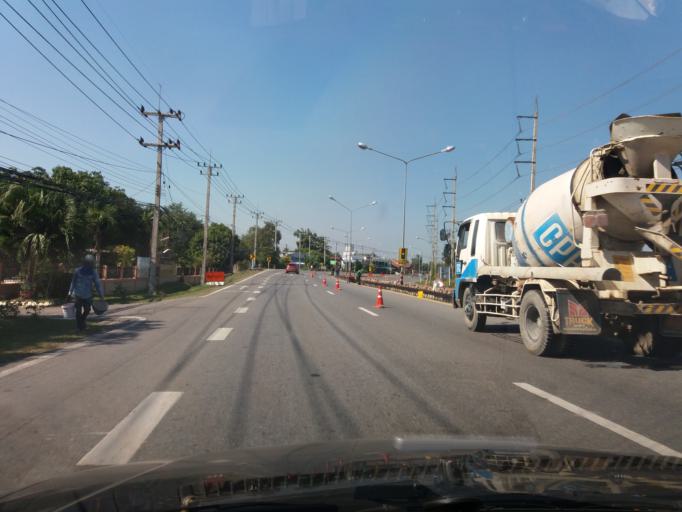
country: TH
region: Chai Nat
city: Manorom
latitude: 15.2610
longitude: 100.0927
